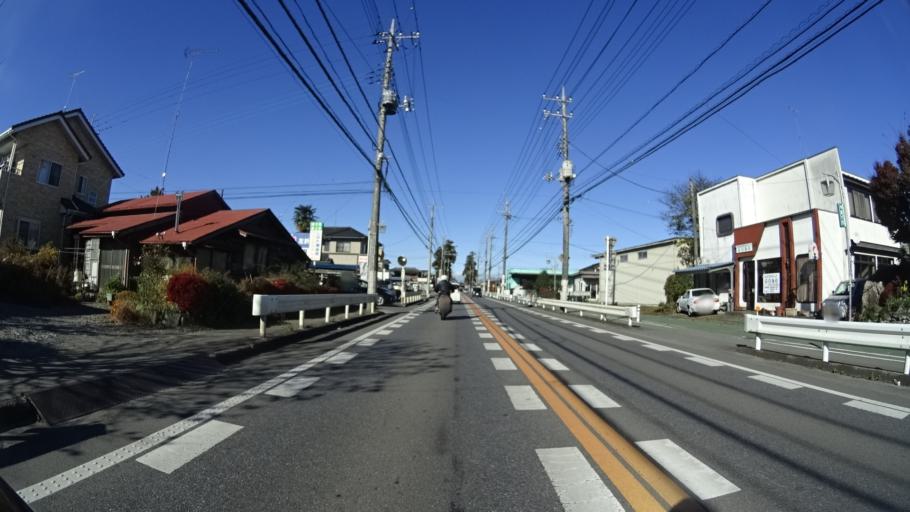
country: JP
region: Tochigi
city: Kanuma
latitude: 36.5346
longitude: 139.7473
